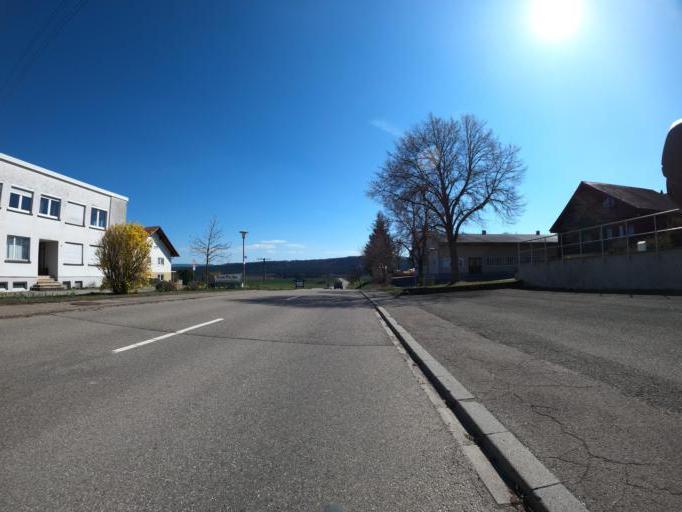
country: DE
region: Baden-Wuerttemberg
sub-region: Tuebingen Region
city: Rangendingen
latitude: 48.3866
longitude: 8.8475
